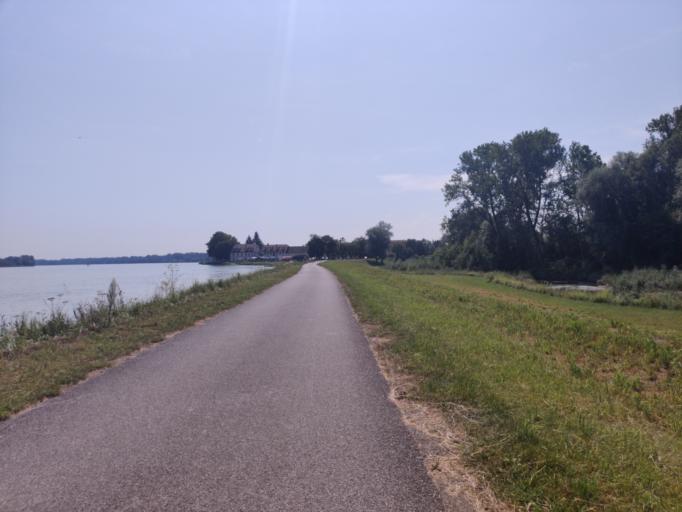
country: AT
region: Upper Austria
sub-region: Politischer Bezirk Urfahr-Umgebung
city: Feldkirchen an der Donau
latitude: 48.3392
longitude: 14.0224
